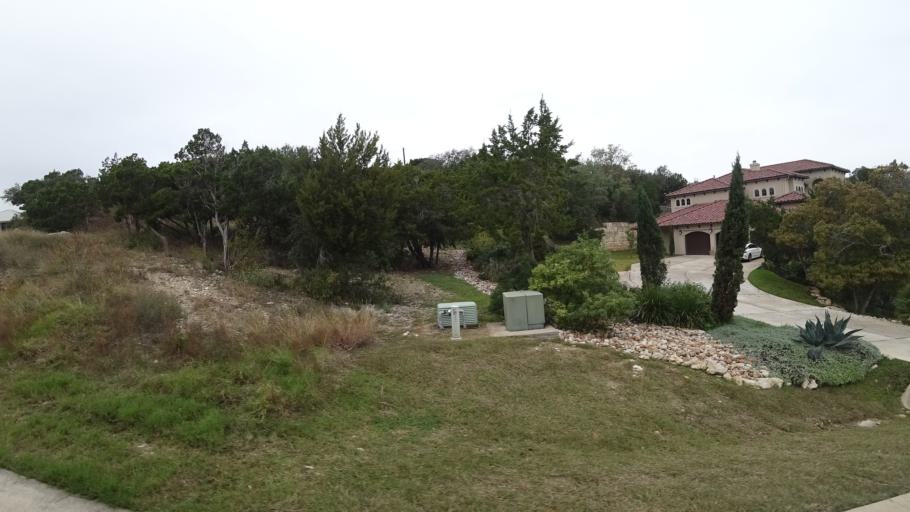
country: US
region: Texas
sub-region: Travis County
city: Hudson Bend
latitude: 30.3917
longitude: -97.9178
